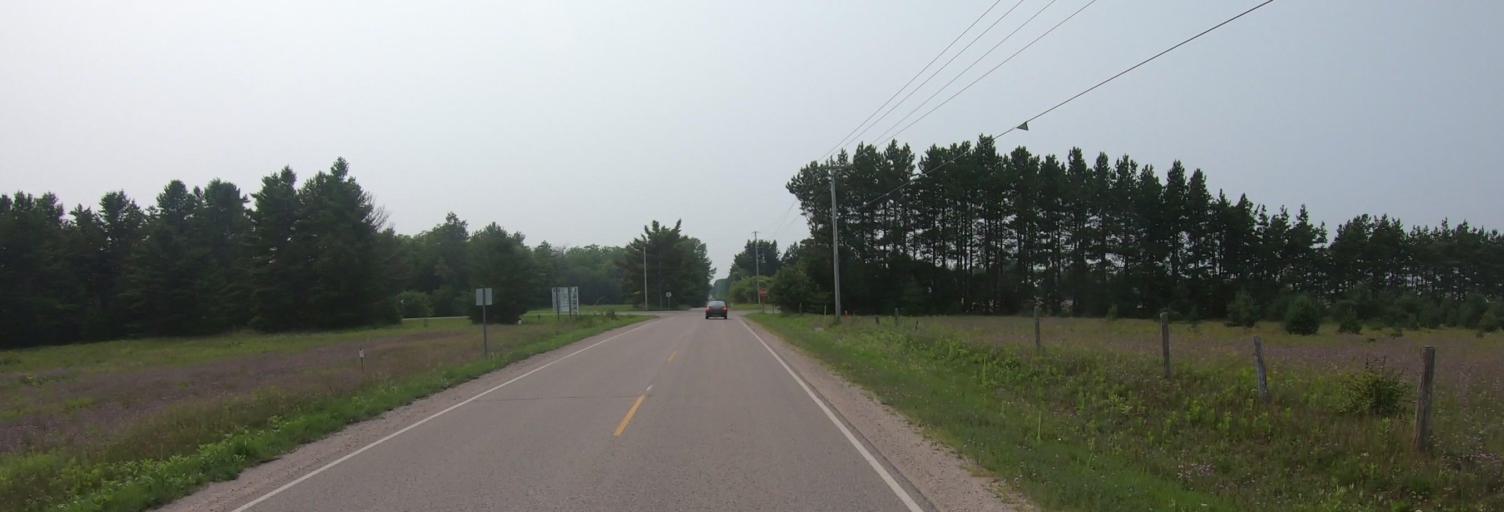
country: US
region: Michigan
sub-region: Cheboygan County
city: Cheboygan
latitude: 46.0145
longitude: -84.0703
